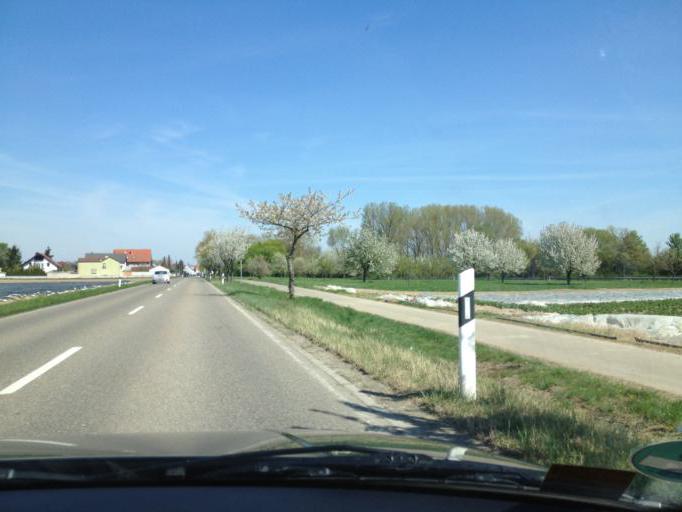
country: DE
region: Rheinland-Pfalz
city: Otterstadt
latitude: 49.3812
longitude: 8.4372
